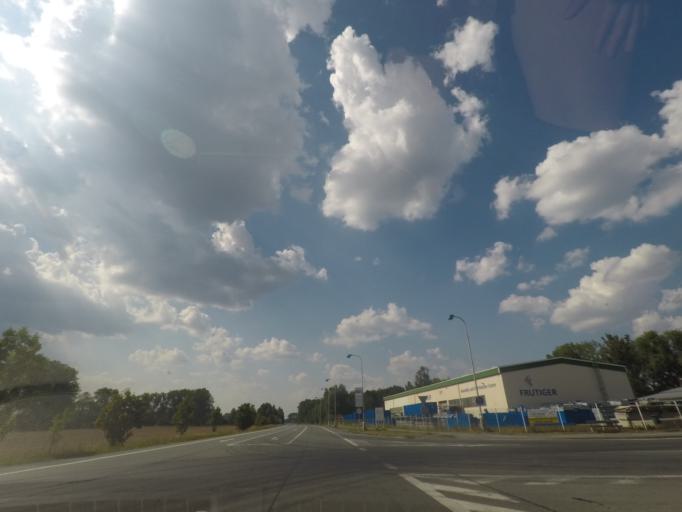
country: CZ
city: Tyniste nad Orlici
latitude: 50.1577
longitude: 16.0633
